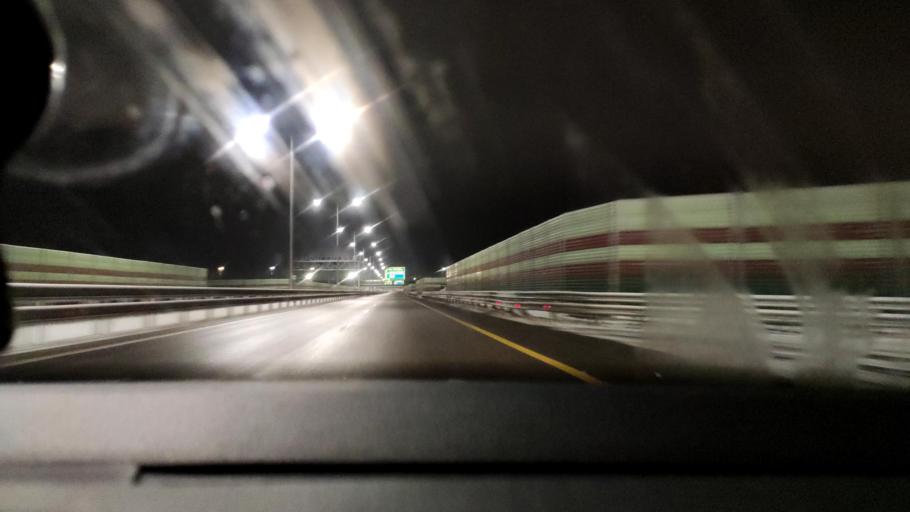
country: RU
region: Moskovskaya
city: Solnechnogorsk
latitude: 56.1510
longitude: 36.9246
